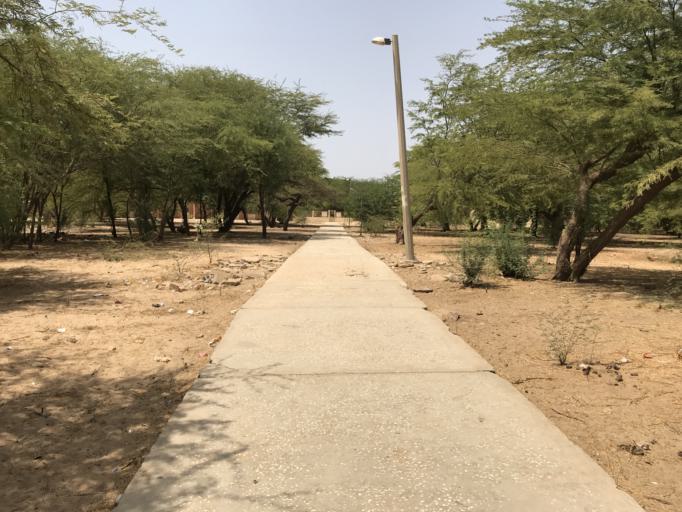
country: SN
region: Saint-Louis
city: Saint-Louis
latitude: 16.0625
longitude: -16.4249
